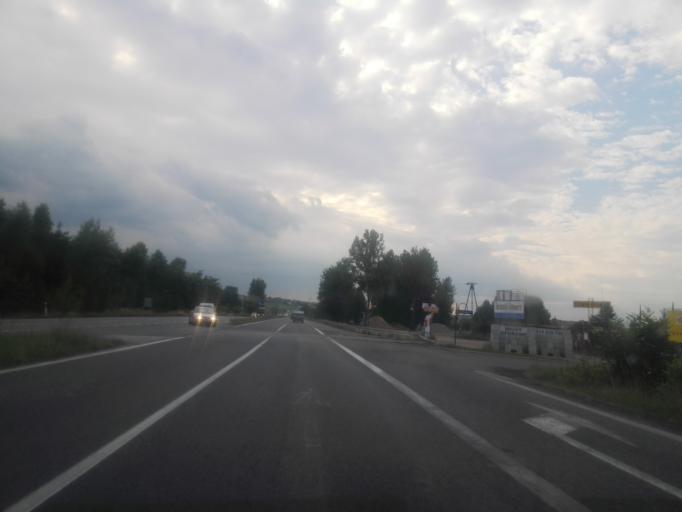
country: PL
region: Silesian Voivodeship
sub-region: Powiat bedzinski
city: Siewierz
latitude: 50.4877
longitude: 19.2154
